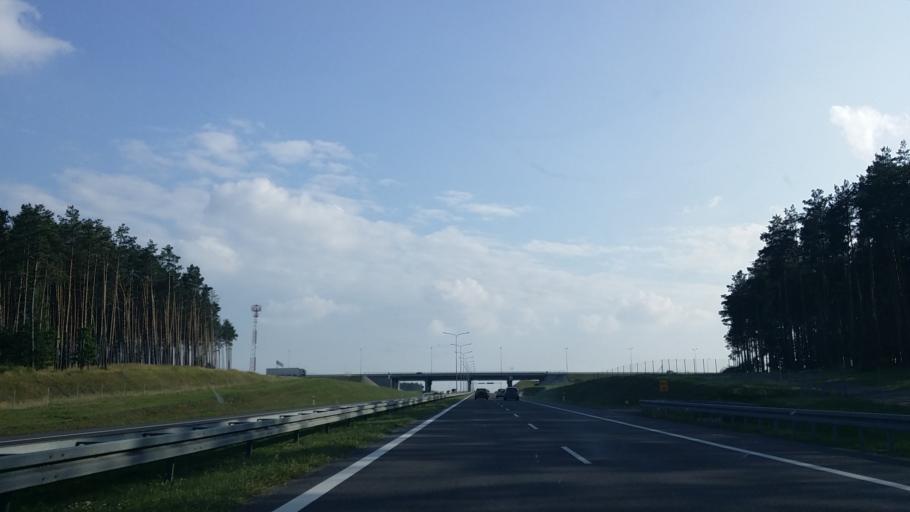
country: PL
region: Lubusz
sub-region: Powiat swiebodzinski
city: Swiebodzin
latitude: 52.3269
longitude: 15.5539
